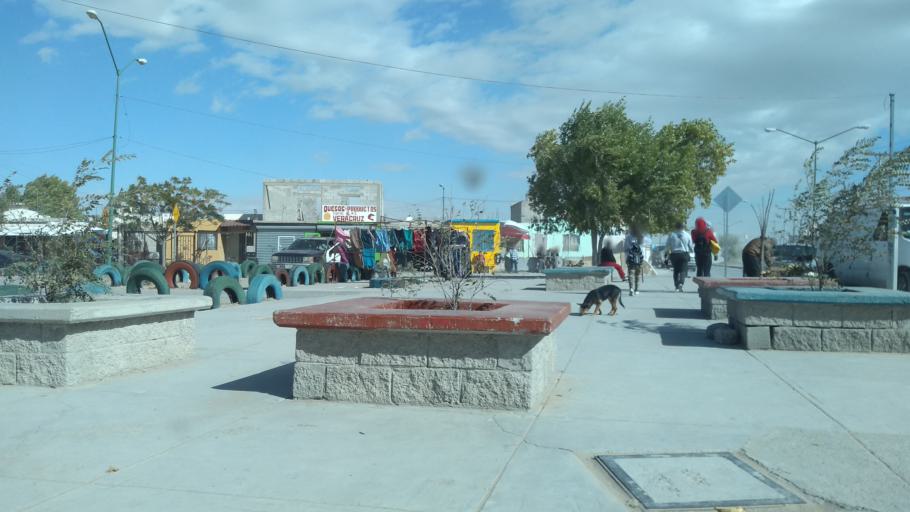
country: US
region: Texas
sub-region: El Paso County
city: Socorro Mission Number 1 Colonia
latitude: 31.5861
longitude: -106.3554
